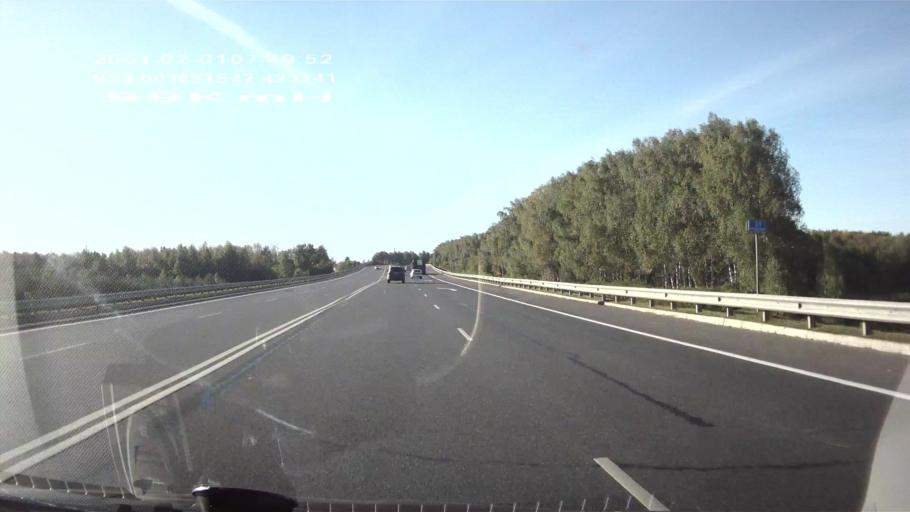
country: RU
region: Chuvashia
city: Shikhazany
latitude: 55.6018
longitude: 47.4237
